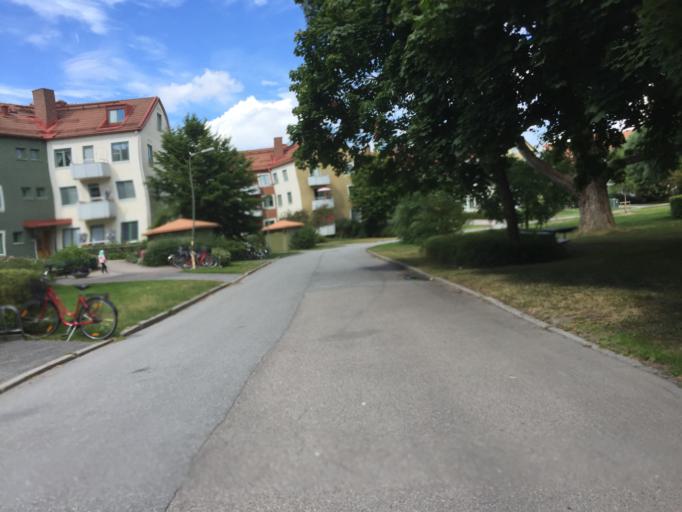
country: SE
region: OErebro
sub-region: Orebro Kommun
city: Orebro
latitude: 59.2717
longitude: 15.1817
